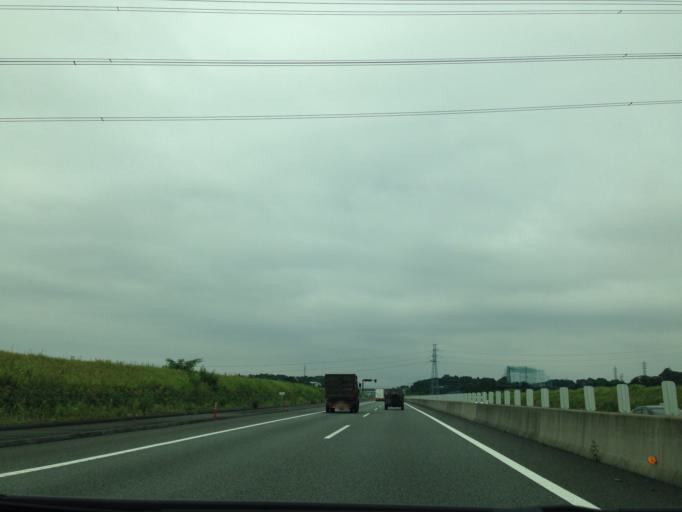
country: JP
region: Shizuoka
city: Fuji
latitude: 35.1942
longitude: 138.7066
